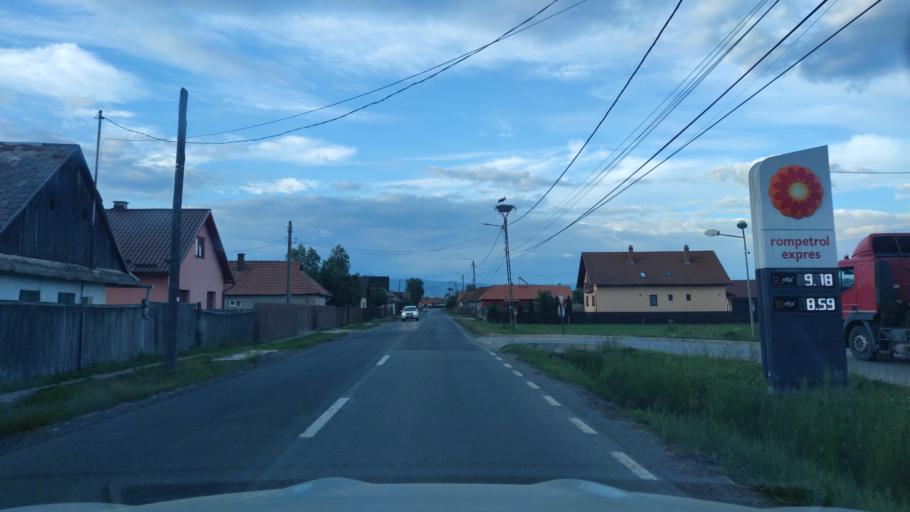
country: RO
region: Harghita
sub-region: Comuna Joseni
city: Joseni
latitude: 46.7010
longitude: 25.4883
